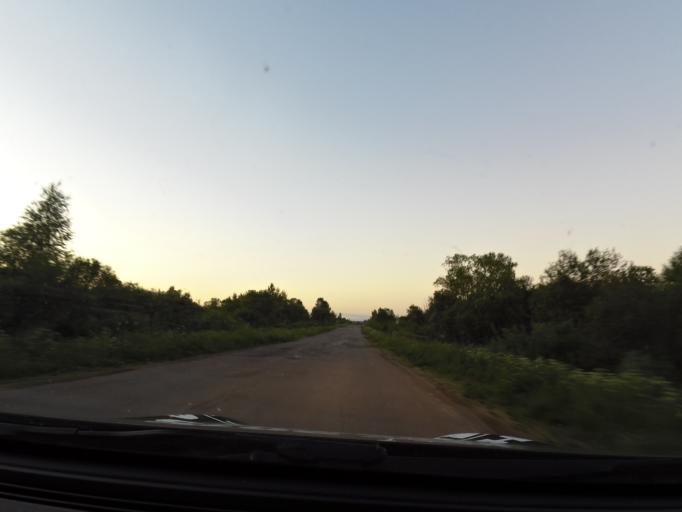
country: RU
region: Vologda
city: Vytegra
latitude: 60.8687
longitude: 36.0076
